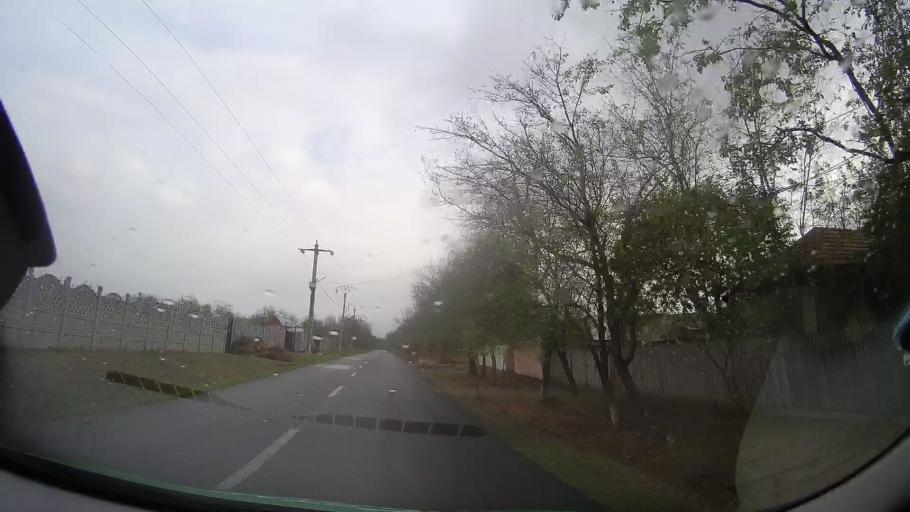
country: RO
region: Ialomita
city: Brazii
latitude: 44.7808
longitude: 26.3260
